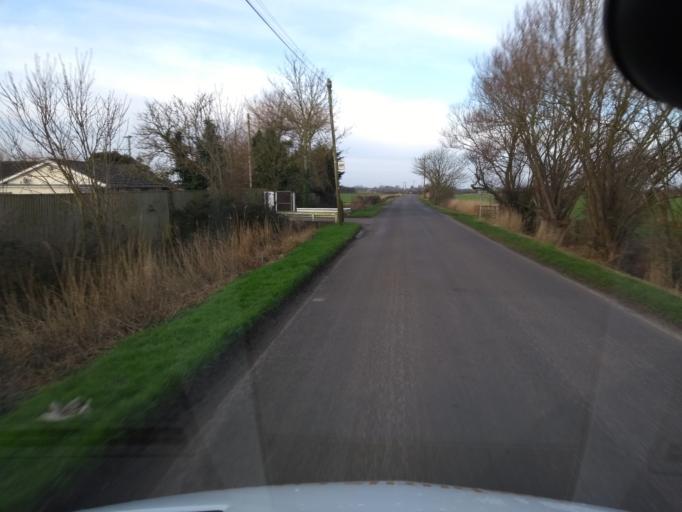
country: GB
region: England
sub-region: Somerset
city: Burnham-on-Sea
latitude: 51.2601
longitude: -2.9883
